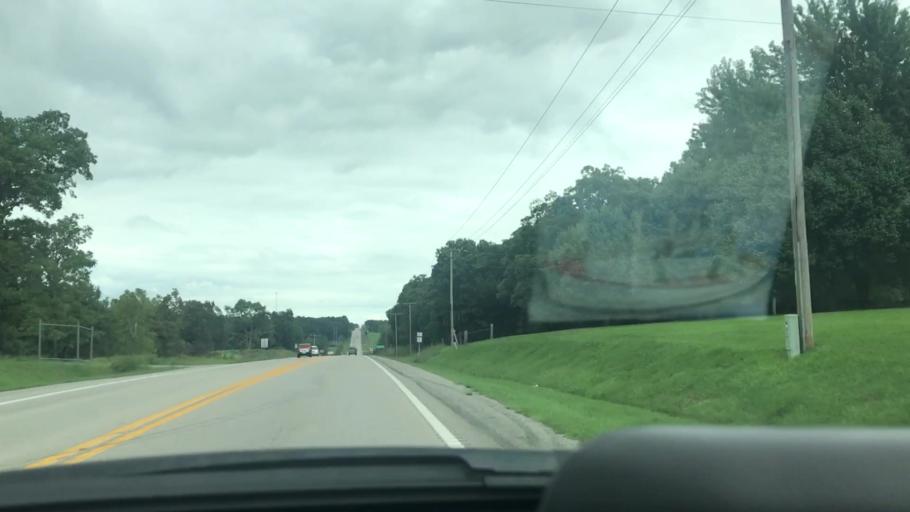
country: US
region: Missouri
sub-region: Dallas County
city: Buffalo
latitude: 37.6739
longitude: -93.1032
